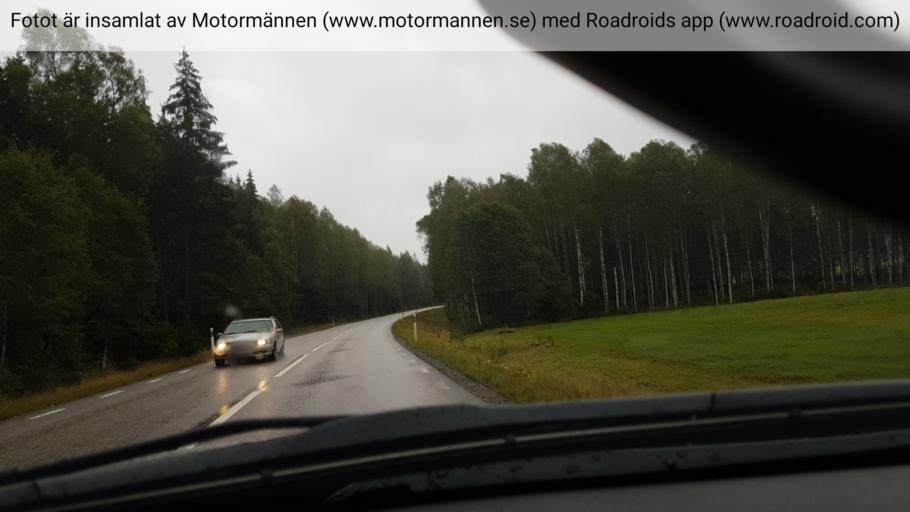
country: SE
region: Vaestra Goetaland
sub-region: Bengtsfors Kommun
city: Dals Langed
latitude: 58.8555
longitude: 12.1717
